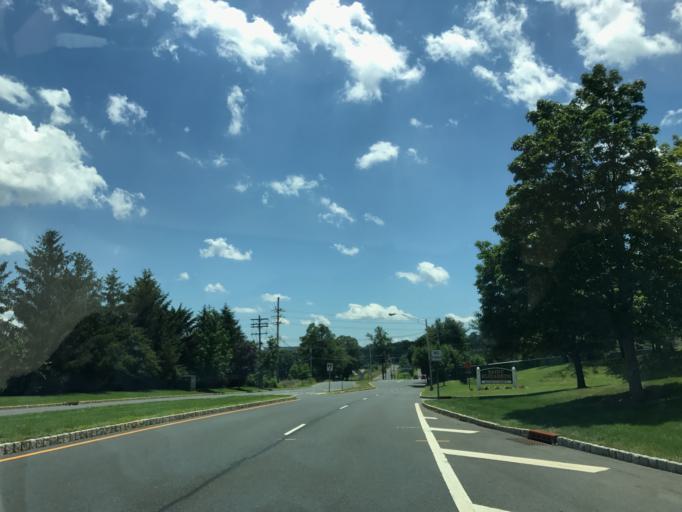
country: US
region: New Jersey
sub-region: Morris County
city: Madison
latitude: 40.7819
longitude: -74.4300
